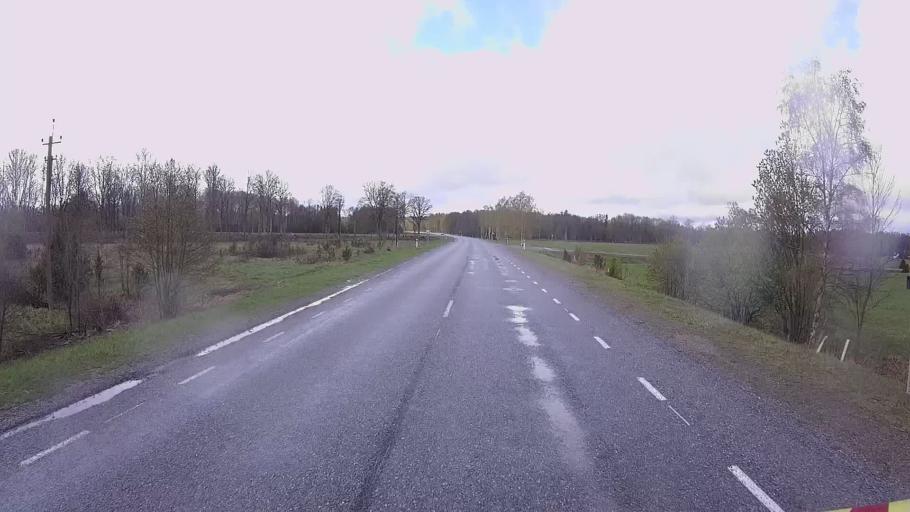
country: EE
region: Hiiumaa
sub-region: Kaerdla linn
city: Kardla
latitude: 58.8267
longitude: 22.7546
